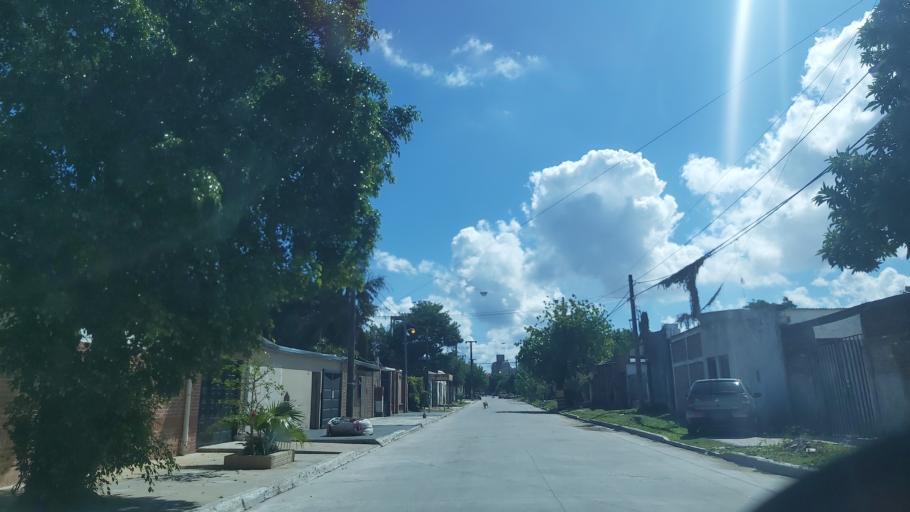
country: AR
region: Corrientes
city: Corrientes
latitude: -27.4801
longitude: -58.8503
